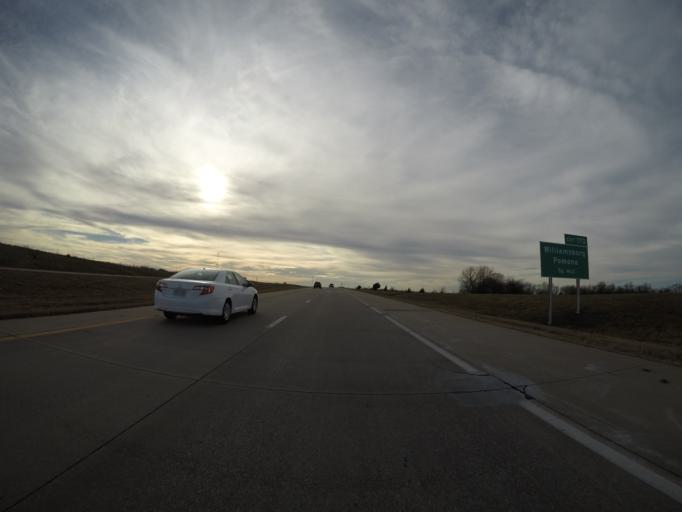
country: US
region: Kansas
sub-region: Franklin County
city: Ottawa
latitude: 38.4967
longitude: -95.4591
